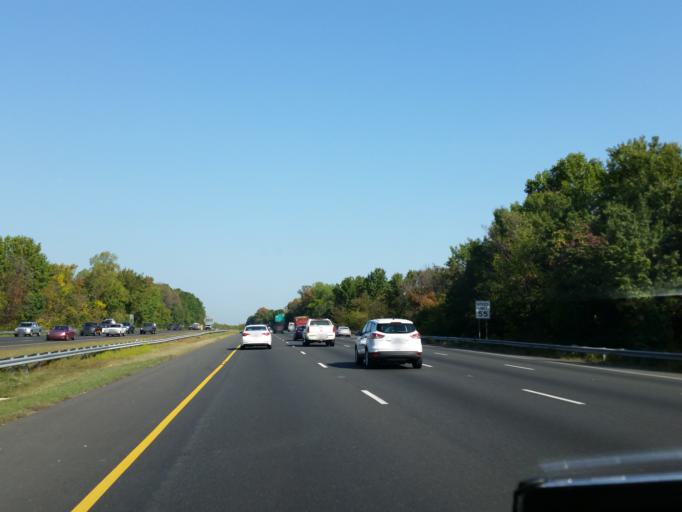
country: US
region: Maryland
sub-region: Prince George's County
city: Largo
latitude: 38.8779
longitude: -76.8437
